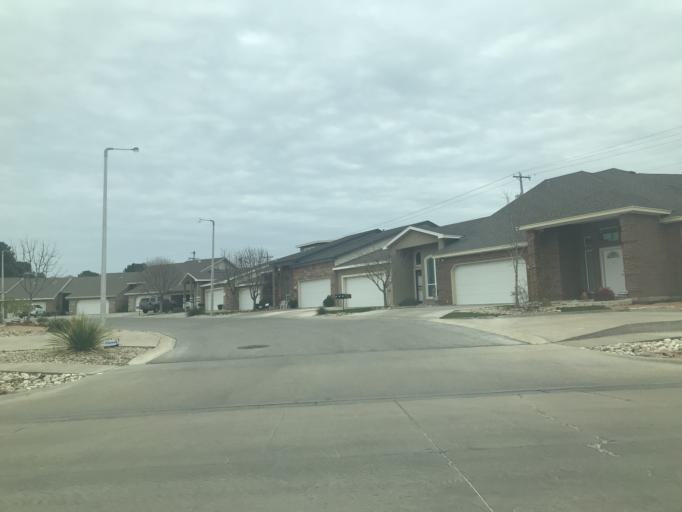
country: US
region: Texas
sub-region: Tom Green County
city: San Angelo
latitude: 31.4185
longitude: -100.4769
